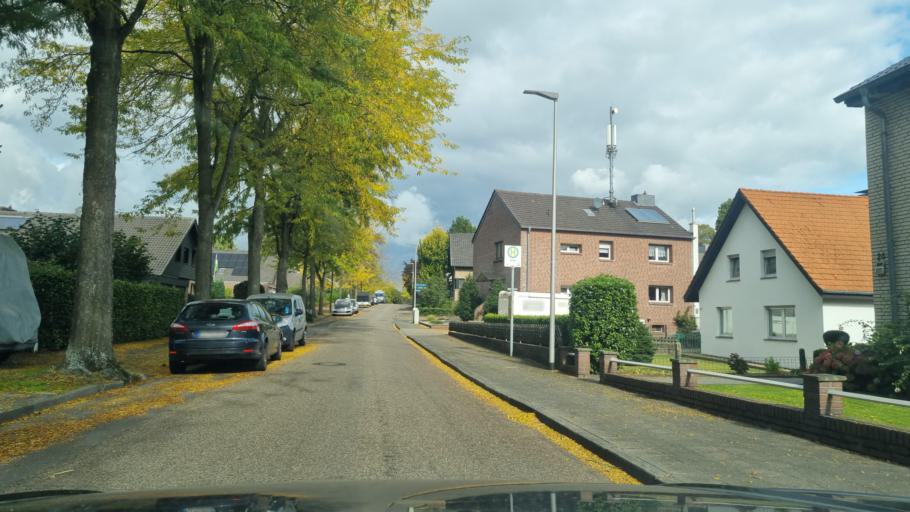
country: DE
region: North Rhine-Westphalia
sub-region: Regierungsbezirk Dusseldorf
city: Kleve
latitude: 51.7796
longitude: 6.1037
